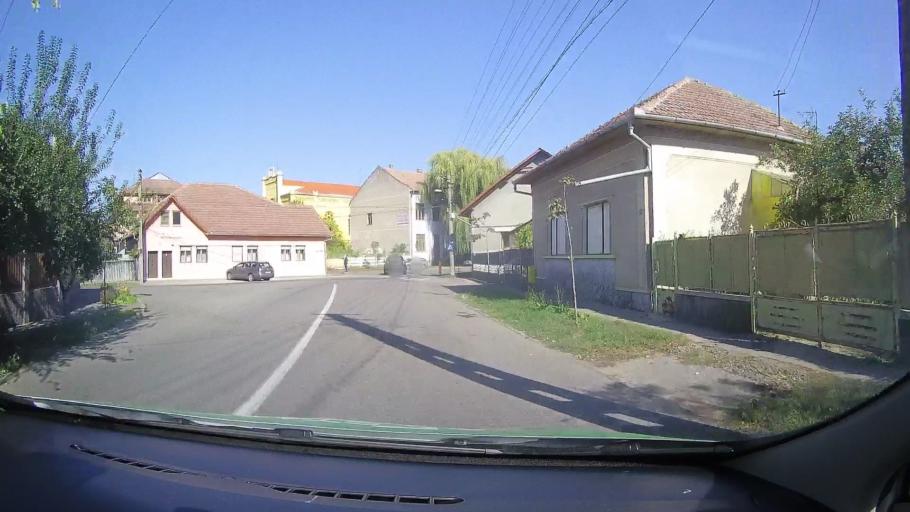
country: RO
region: Satu Mare
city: Carei
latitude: 47.6840
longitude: 22.4633
